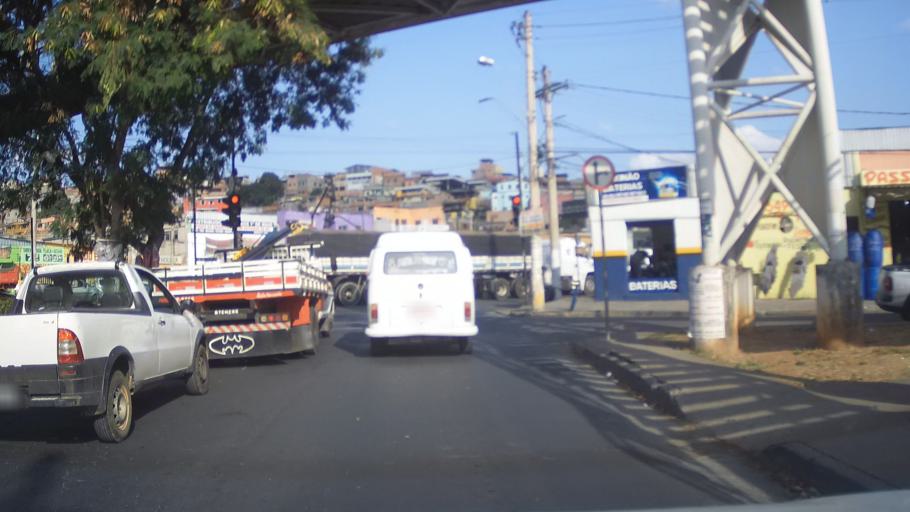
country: BR
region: Minas Gerais
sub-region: Belo Horizonte
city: Belo Horizonte
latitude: -19.8601
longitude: -43.9339
